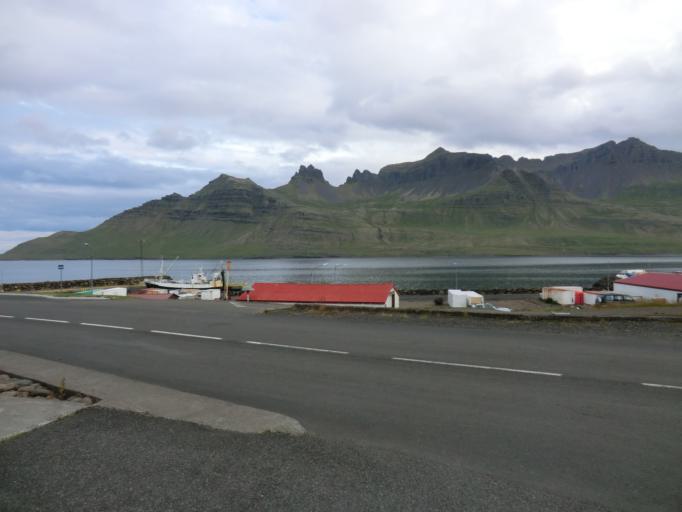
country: IS
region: East
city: Eskifjoerdur
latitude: 64.8335
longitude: -13.8756
